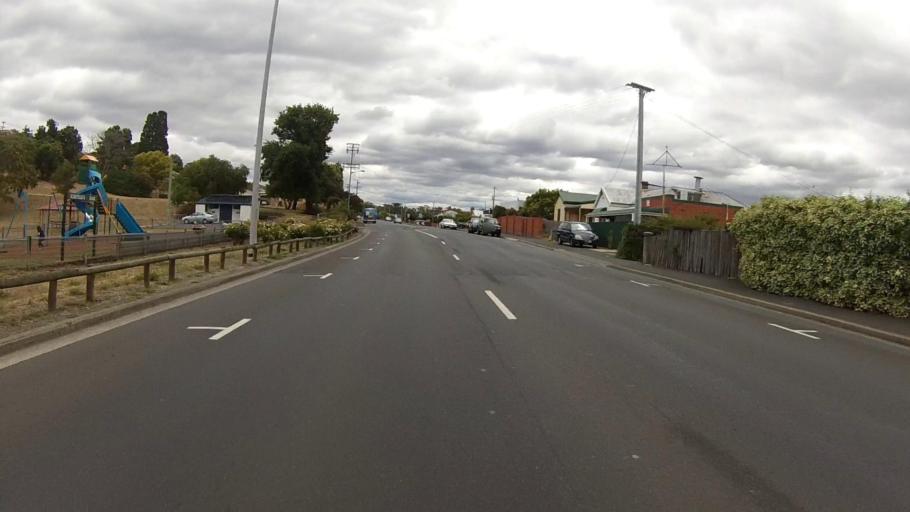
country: AU
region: Tasmania
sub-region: Glenorchy
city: Claremont
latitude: -42.7824
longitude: 147.2523
